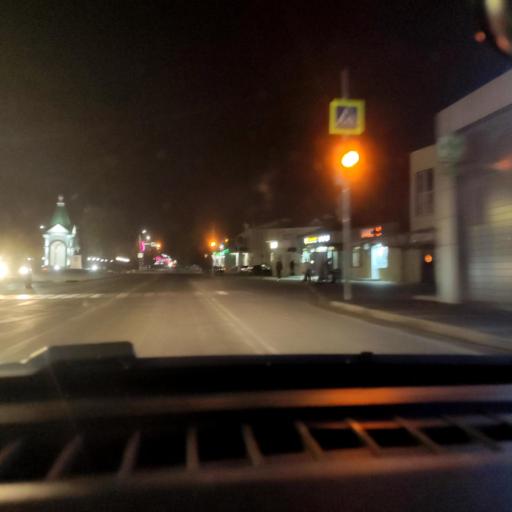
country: RU
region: Voronezj
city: Novaya Usman'
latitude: 51.6429
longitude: 39.4104
